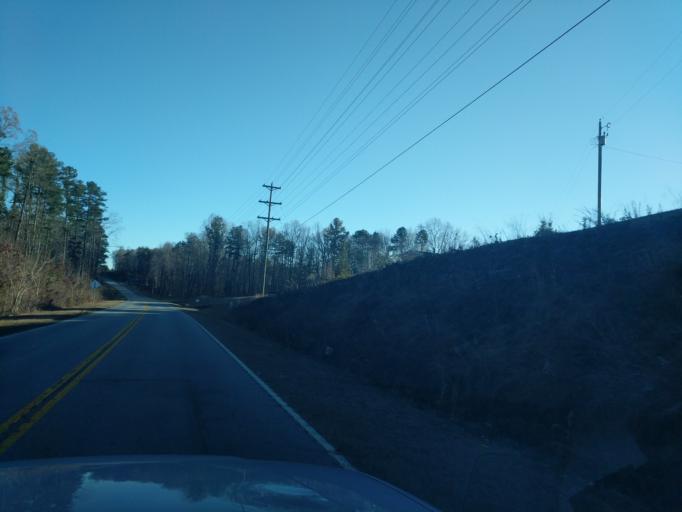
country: US
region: South Carolina
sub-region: Oconee County
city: Westminster
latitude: 34.6980
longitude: -83.1867
